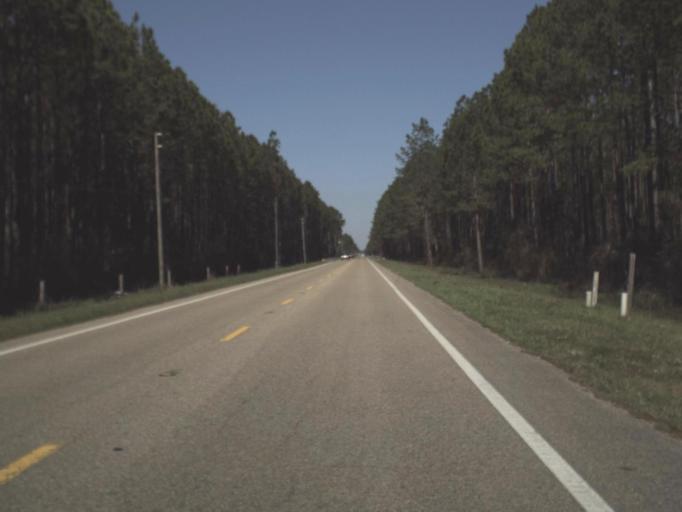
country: US
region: Florida
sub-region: Gulf County
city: Port Saint Joe
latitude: 29.8464
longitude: -85.2623
